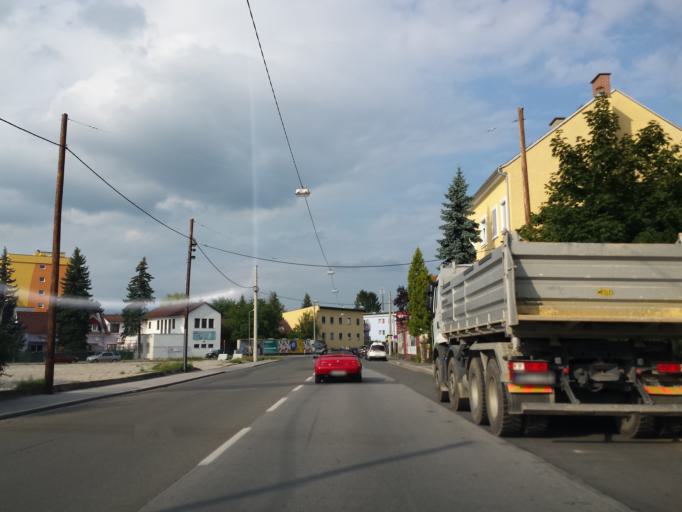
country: AT
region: Styria
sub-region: Graz Stadt
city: Wetzelsdorf
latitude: 47.0622
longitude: 15.3982
